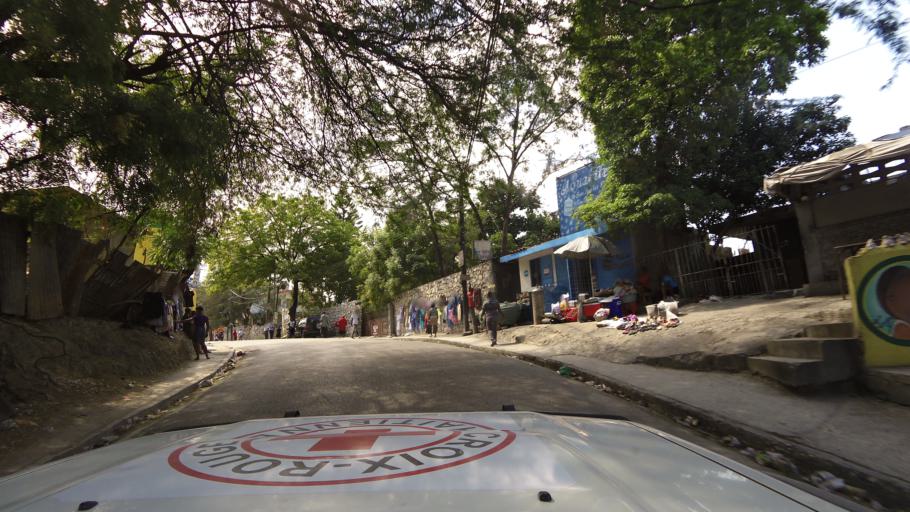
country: HT
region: Ouest
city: Delmas 73
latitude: 18.5373
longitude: -72.2964
